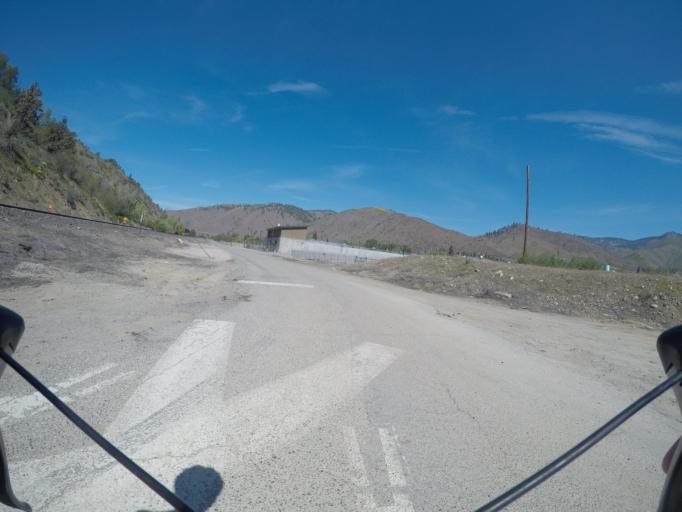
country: US
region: Washington
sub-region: Chelan County
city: Cashmere
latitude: 47.5092
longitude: -120.4506
